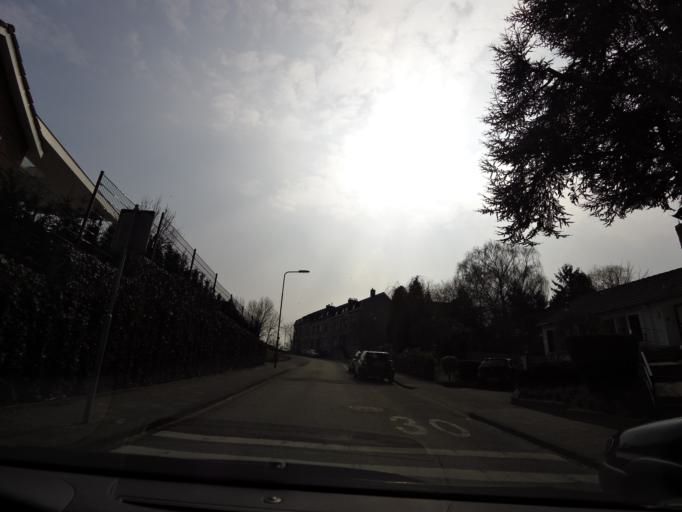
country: NL
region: Limburg
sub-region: Gemeente Simpelveld
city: Simpelveld
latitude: 50.8316
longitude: 5.9730
